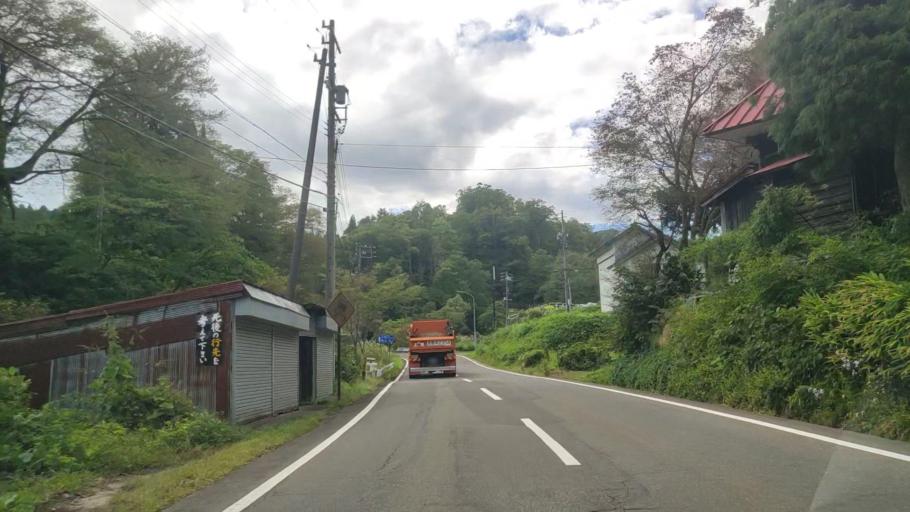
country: JP
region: Nagano
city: Iiyama
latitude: 36.8829
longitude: 138.3206
